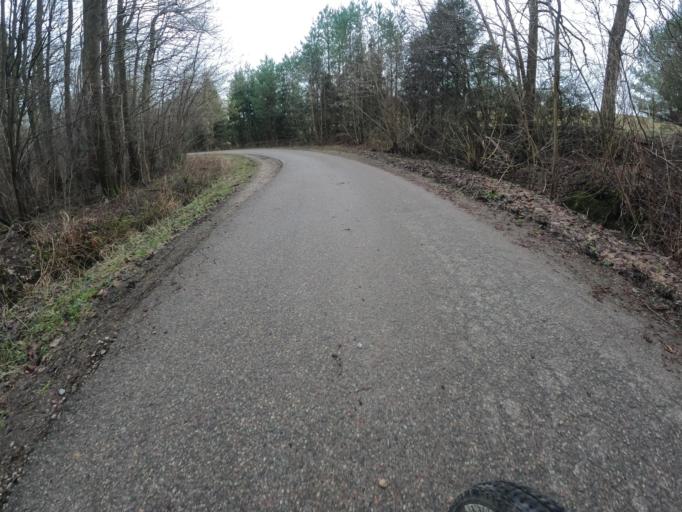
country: PL
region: West Pomeranian Voivodeship
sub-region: Powiat slawienski
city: Slawno
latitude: 54.2566
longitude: 16.6581
